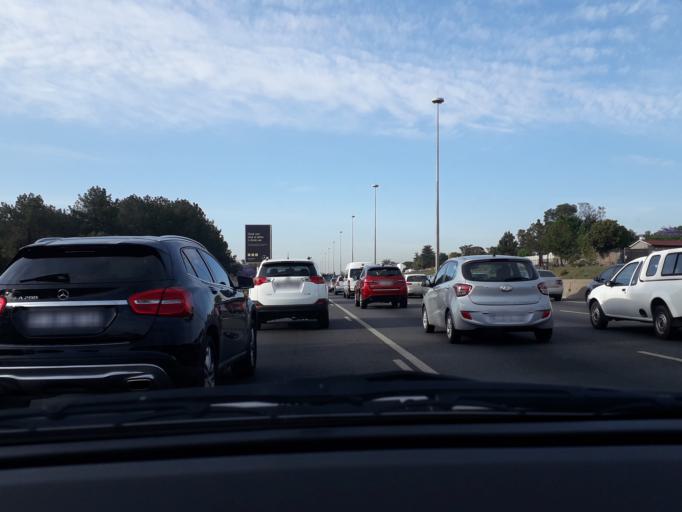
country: ZA
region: Gauteng
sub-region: City of Johannesburg Metropolitan Municipality
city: Modderfontein
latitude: -26.0679
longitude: 28.0901
